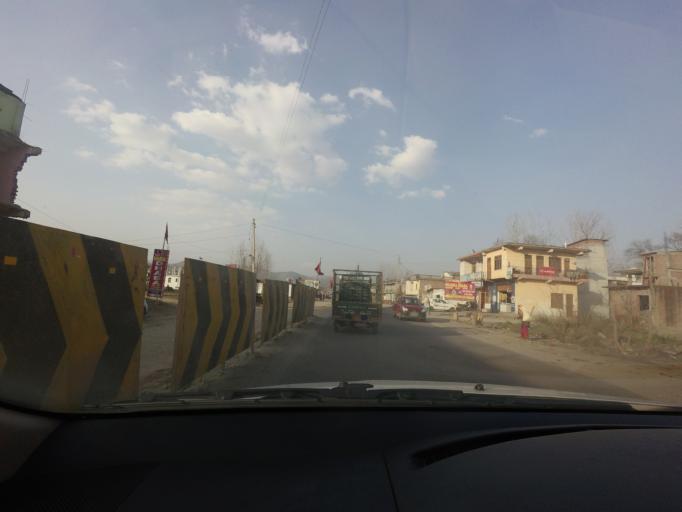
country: IN
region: Himachal Pradesh
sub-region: Mandi
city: Sundarnagar
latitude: 31.5934
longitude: 76.9240
